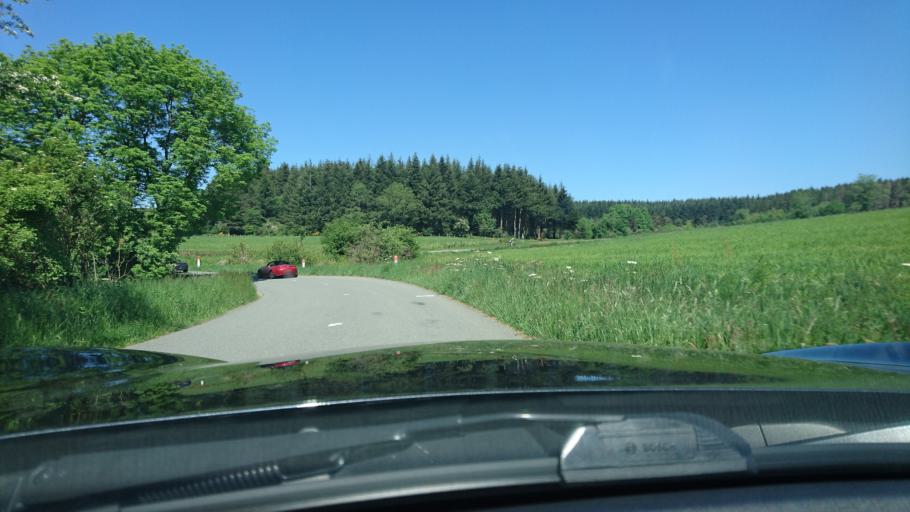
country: FR
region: Rhone-Alpes
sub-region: Departement de la Loire
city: Violay
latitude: 45.8966
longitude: 4.3259
